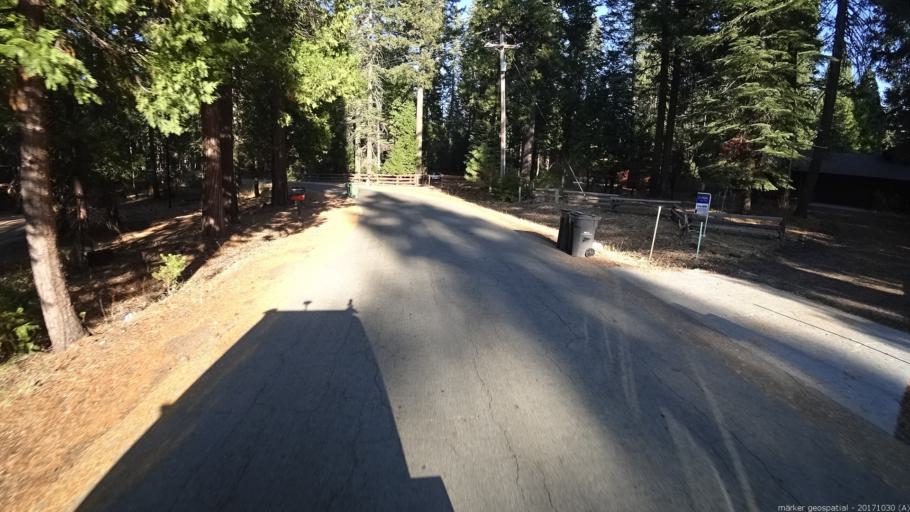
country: US
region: California
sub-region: Shasta County
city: Shingletown
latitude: 40.5559
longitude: -121.7176
